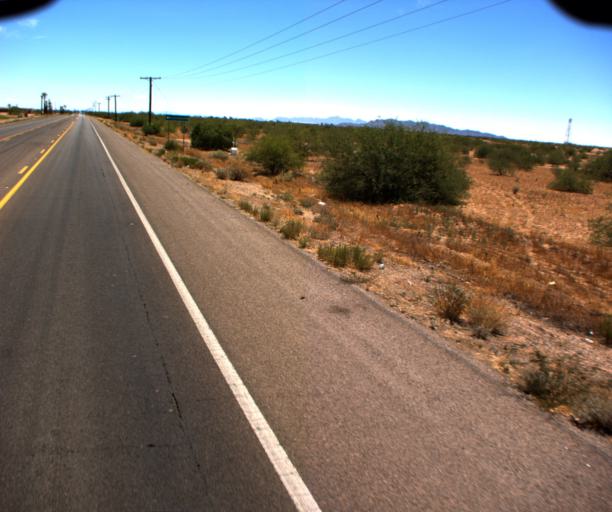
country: US
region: Arizona
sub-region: Pinal County
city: Casa Grande
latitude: 32.8794
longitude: -111.8464
